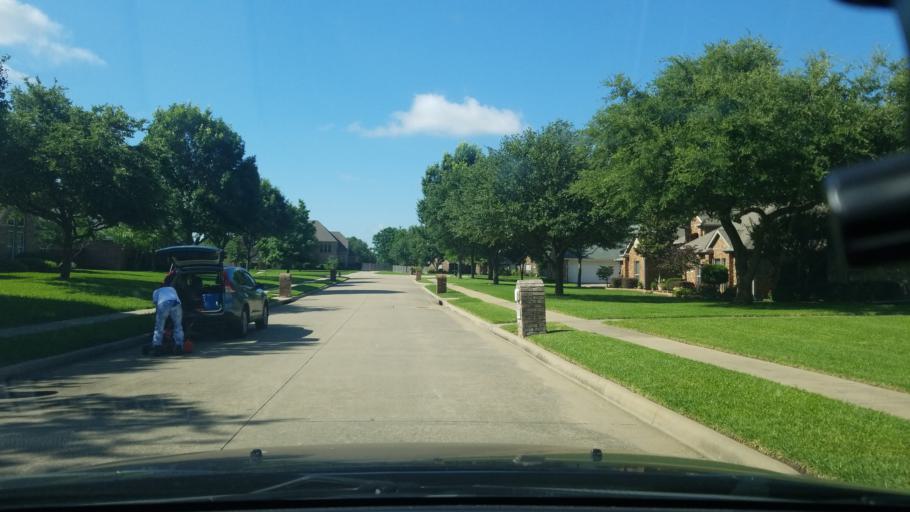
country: US
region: Texas
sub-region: Dallas County
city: Sunnyvale
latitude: 32.8042
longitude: -96.5873
